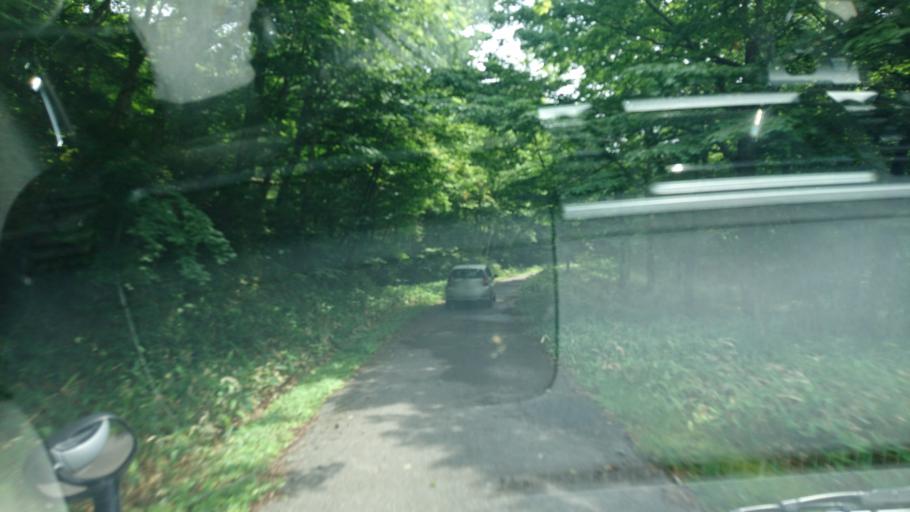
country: JP
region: Iwate
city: Ofunato
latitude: 39.1772
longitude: 141.7813
